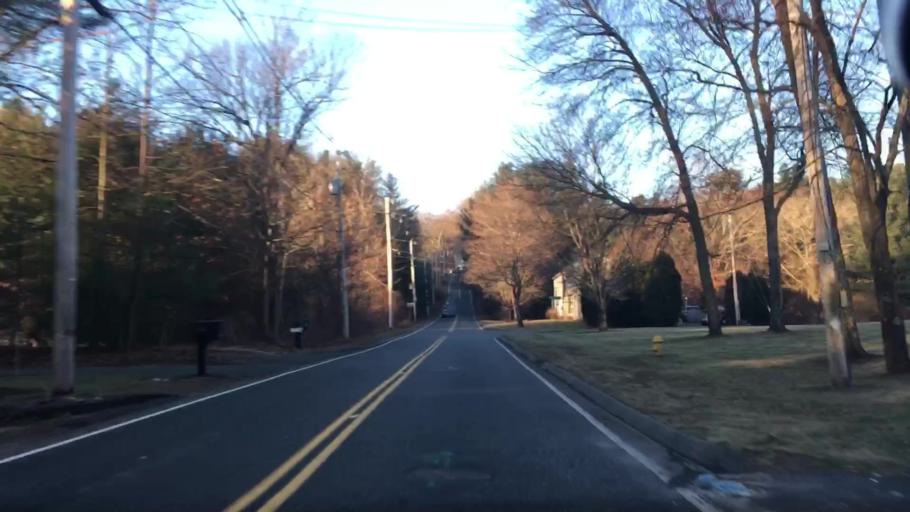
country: US
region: Massachusetts
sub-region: Hampden County
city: East Longmeadow
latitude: 42.0442
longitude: -72.4937
